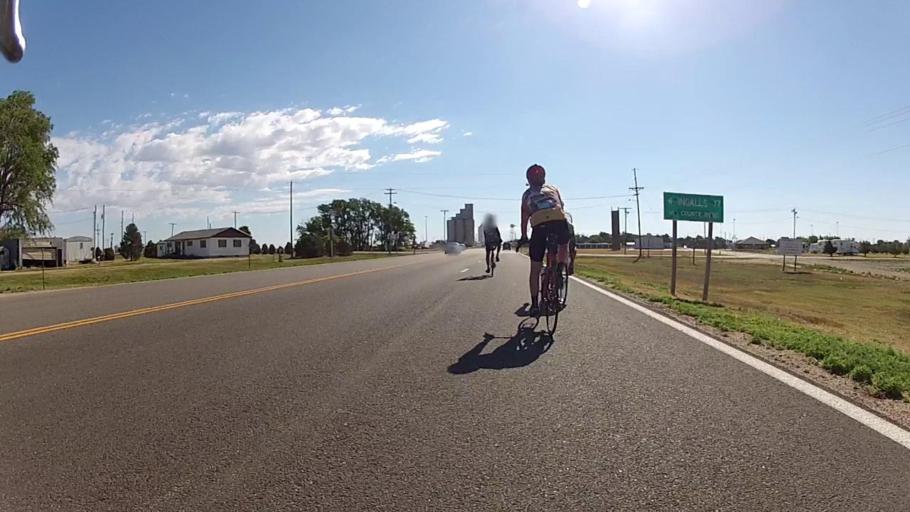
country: US
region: Kansas
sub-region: Gray County
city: Cimarron
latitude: 37.5971
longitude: -100.4523
